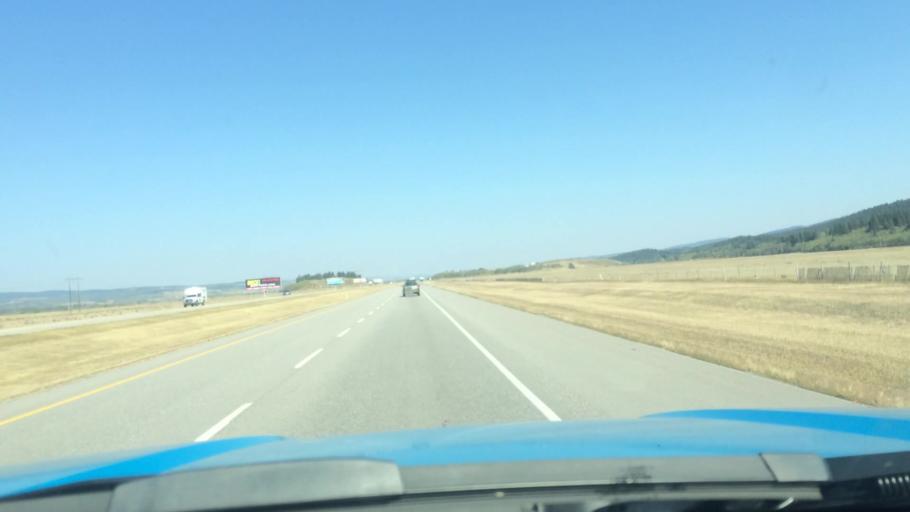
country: CA
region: Alberta
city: Canmore
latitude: 51.1180
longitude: -114.9843
